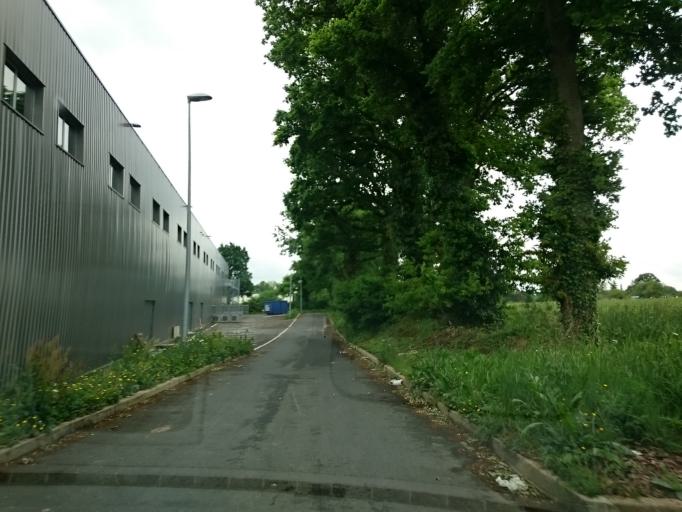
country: FR
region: Brittany
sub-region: Departement d'Ille-et-Vilaine
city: Chantepie
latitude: 48.0635
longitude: -1.6271
